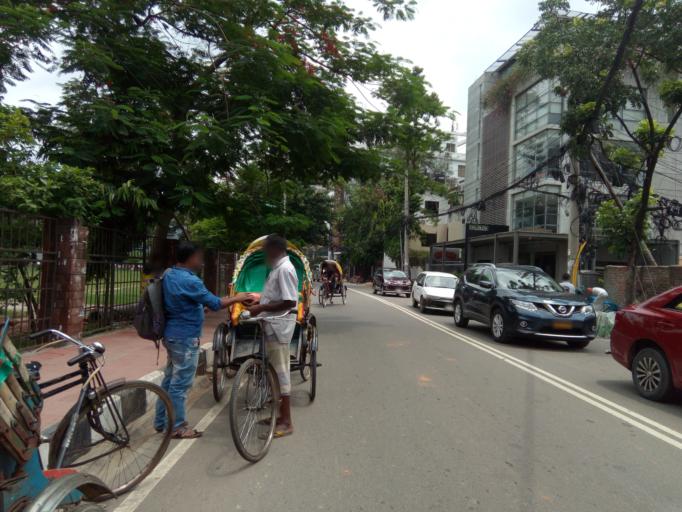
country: BD
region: Dhaka
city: Paltan
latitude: 23.7938
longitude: 90.4086
